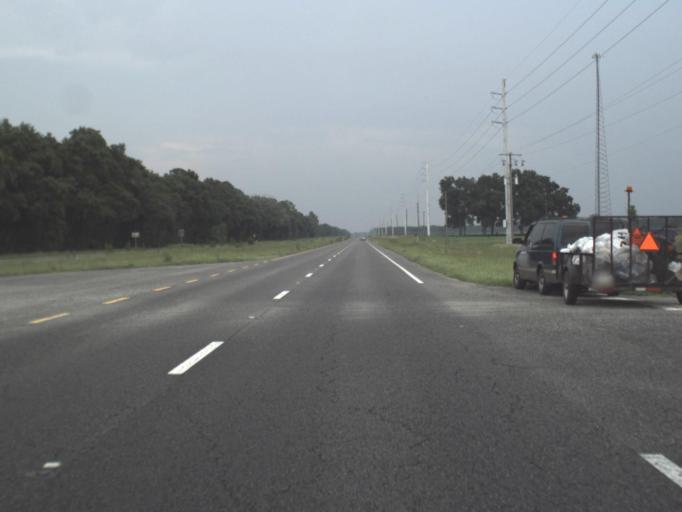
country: US
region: Florida
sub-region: Levy County
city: Chiefland
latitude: 29.4748
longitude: -82.7896
